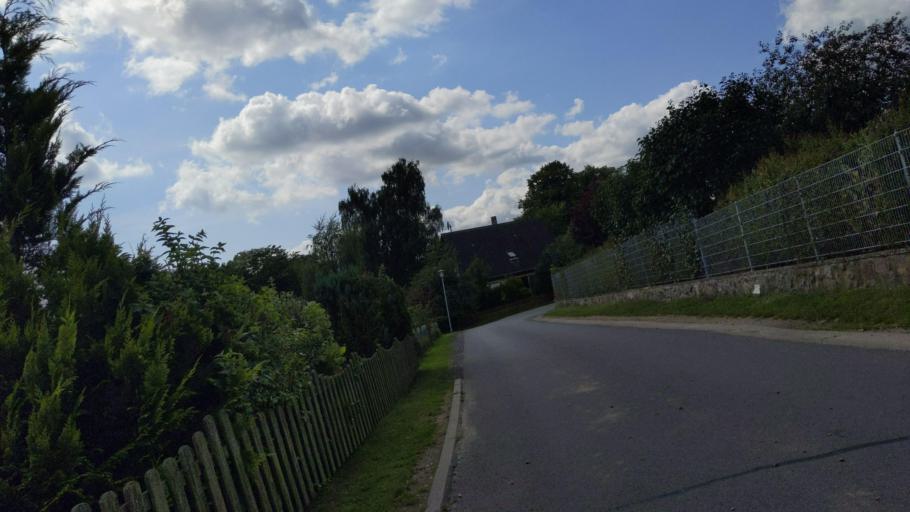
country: DE
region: Schleswig-Holstein
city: Kasseedorf
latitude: 54.1221
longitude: 10.7116
